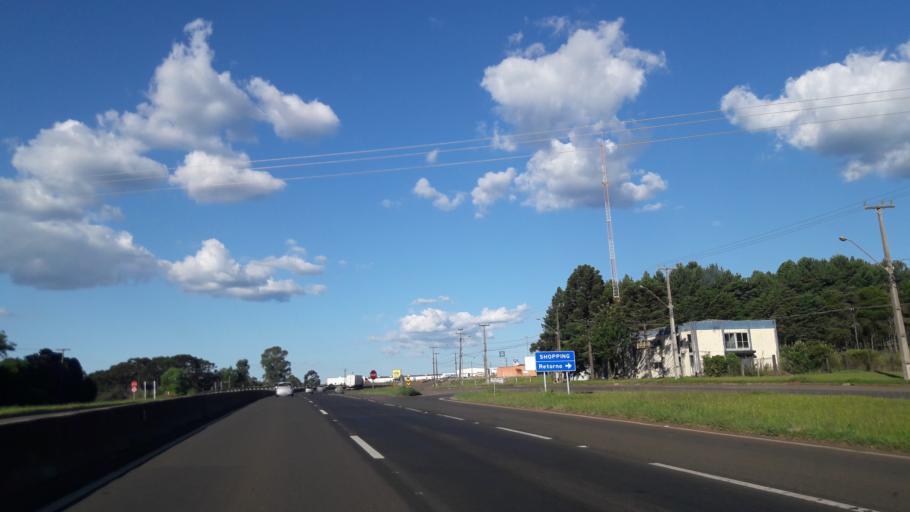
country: BR
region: Parana
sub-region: Guarapuava
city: Guarapuava
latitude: -25.3501
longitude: -51.4566
